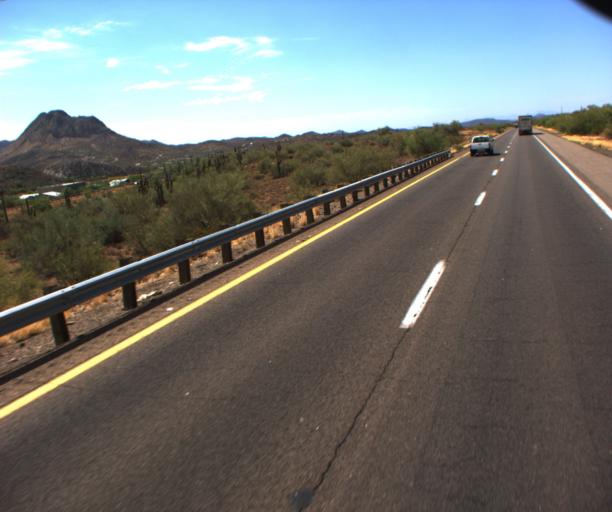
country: US
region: Arizona
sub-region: Maricopa County
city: New River
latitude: 33.9300
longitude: -112.1432
